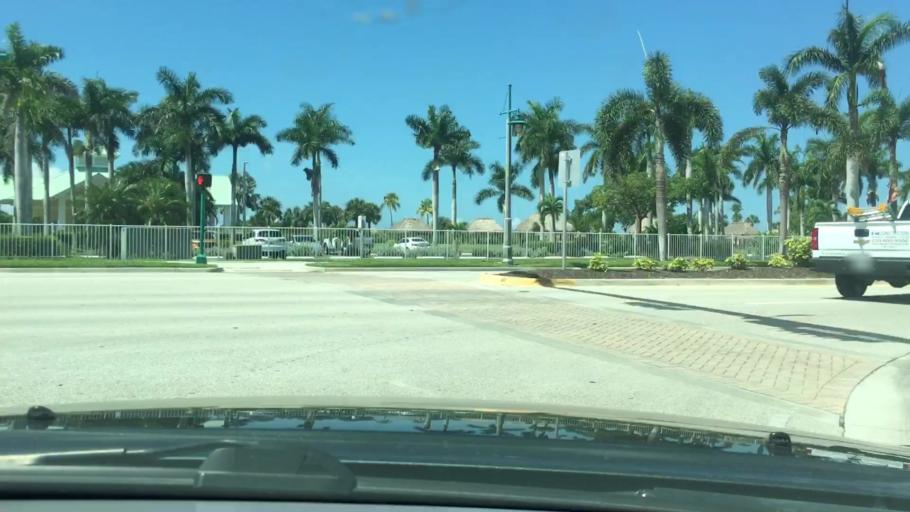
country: US
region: Florida
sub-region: Collier County
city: Marco
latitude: 25.9363
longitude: -81.7315
